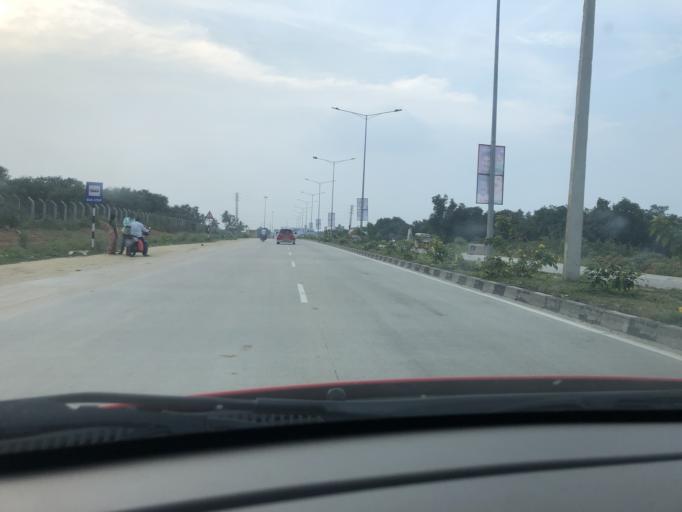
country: IN
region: Andhra Pradesh
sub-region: Chittoor
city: Chittoor
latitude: 13.1944
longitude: 79.0226
